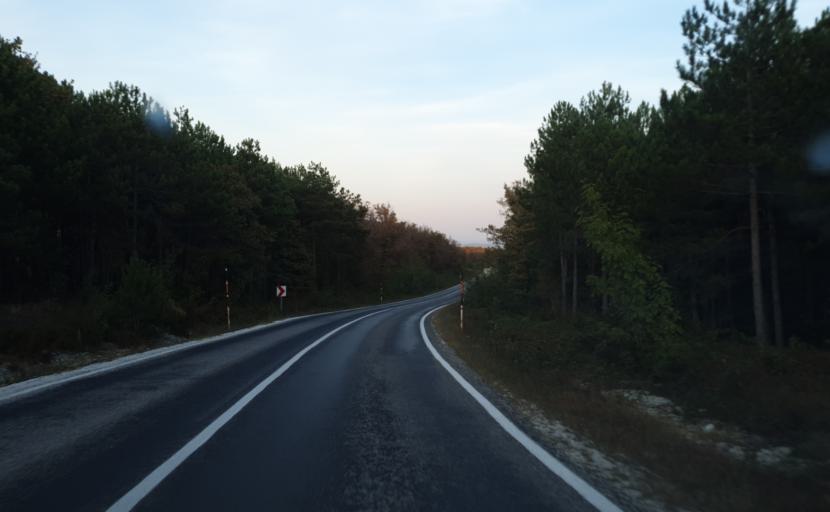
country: TR
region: Kirklareli
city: Igneada
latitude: 41.8616
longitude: 27.8678
